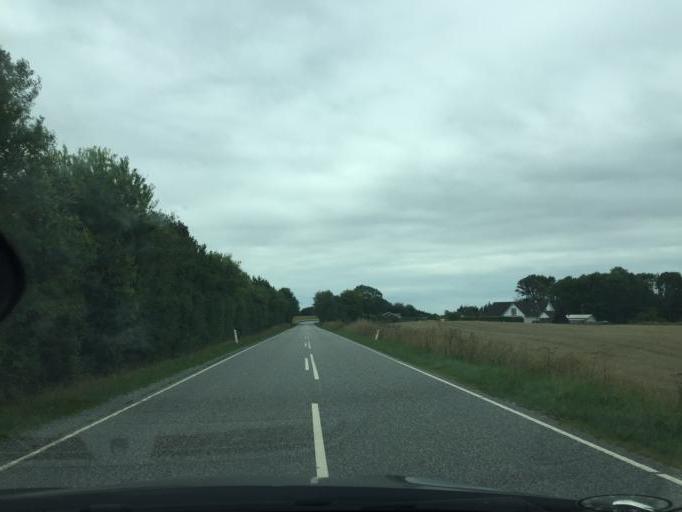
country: DK
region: South Denmark
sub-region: Assens Kommune
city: Vissenbjerg
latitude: 55.3675
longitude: 10.0928
